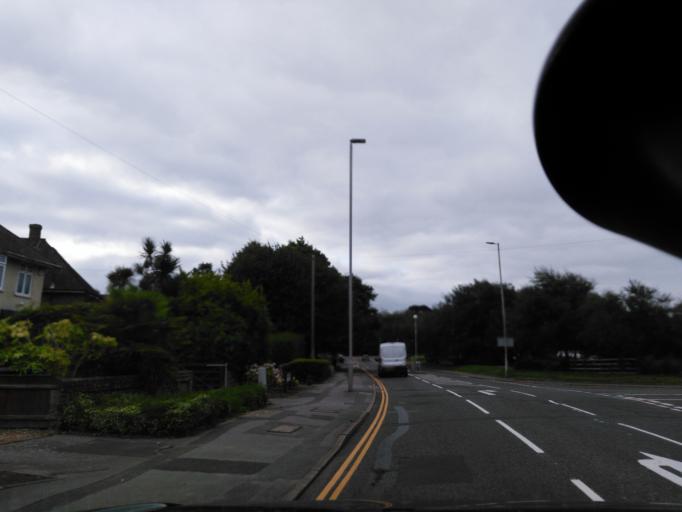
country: GB
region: England
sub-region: Dorset
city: Parkstone
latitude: 50.7165
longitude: -1.9538
